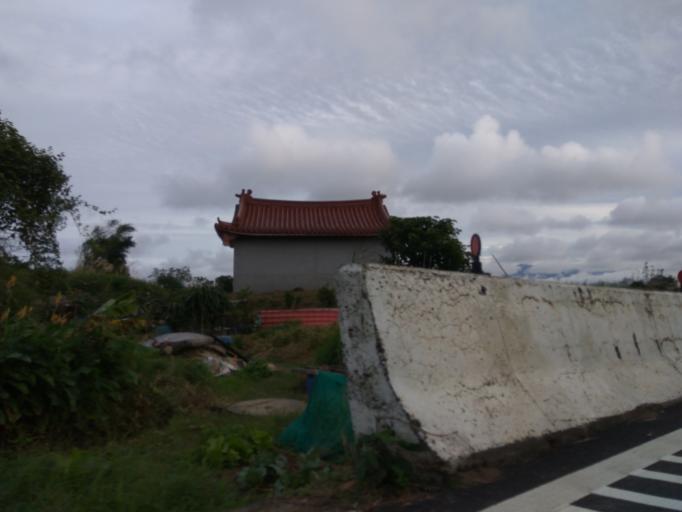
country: TW
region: Taiwan
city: Daxi
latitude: 24.9260
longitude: 121.1970
